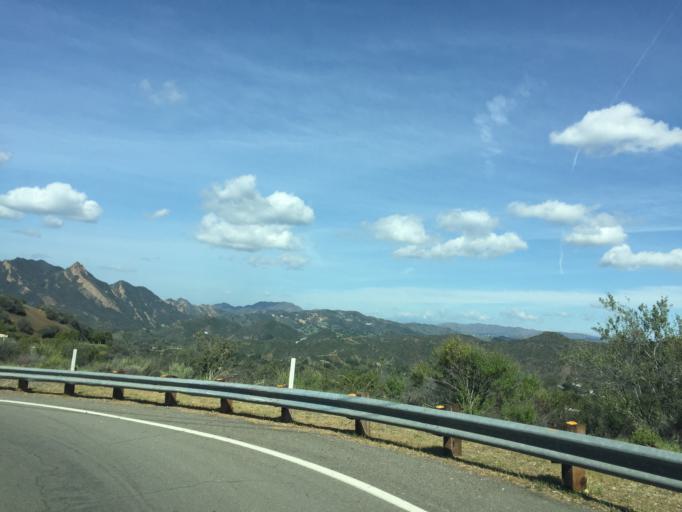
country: US
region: California
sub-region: Los Angeles County
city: Malibu Beach
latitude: 34.0734
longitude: -118.6830
